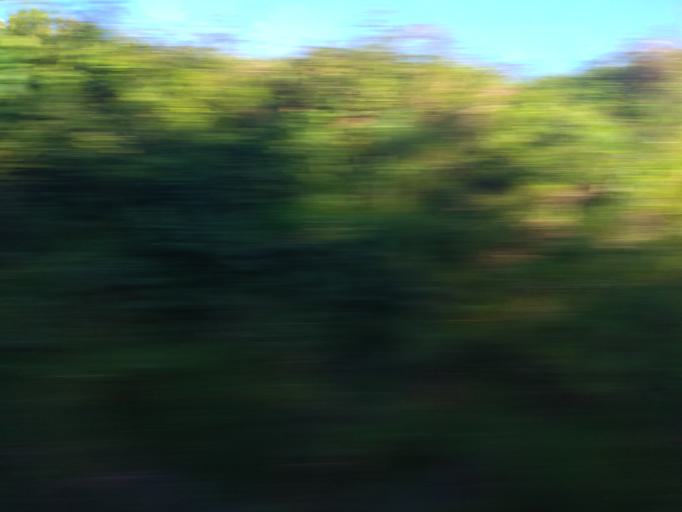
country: FR
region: Rhone-Alpes
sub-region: Departement de la Haute-Savoie
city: Saint-Martin-Bellevue
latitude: 45.9530
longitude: 6.1586
